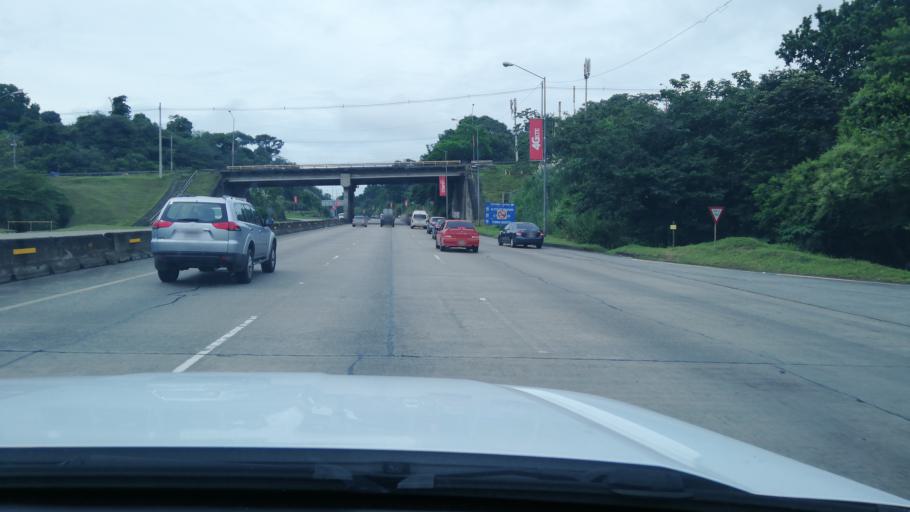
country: PA
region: Panama
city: Panama
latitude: 9.0343
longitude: -79.5359
